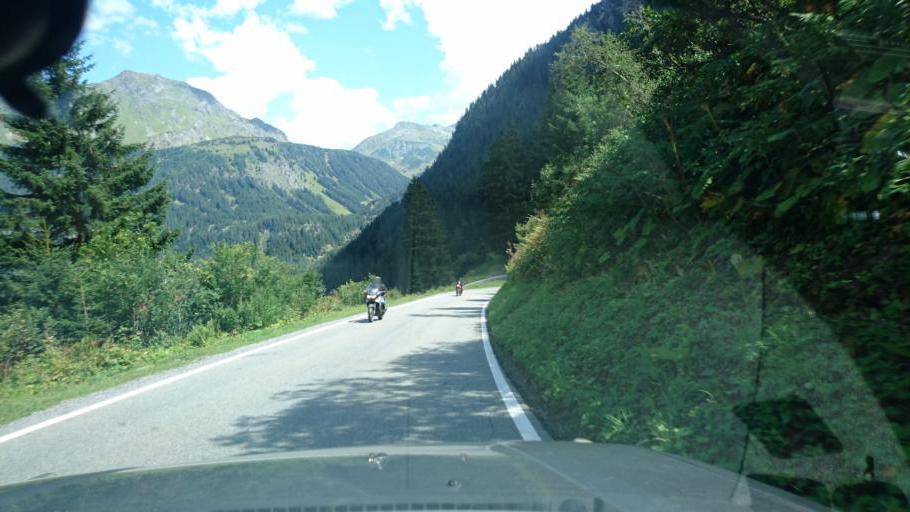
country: AT
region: Vorarlberg
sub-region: Politischer Bezirk Bludenz
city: Gaschurn
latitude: 46.9495
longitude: 10.0696
